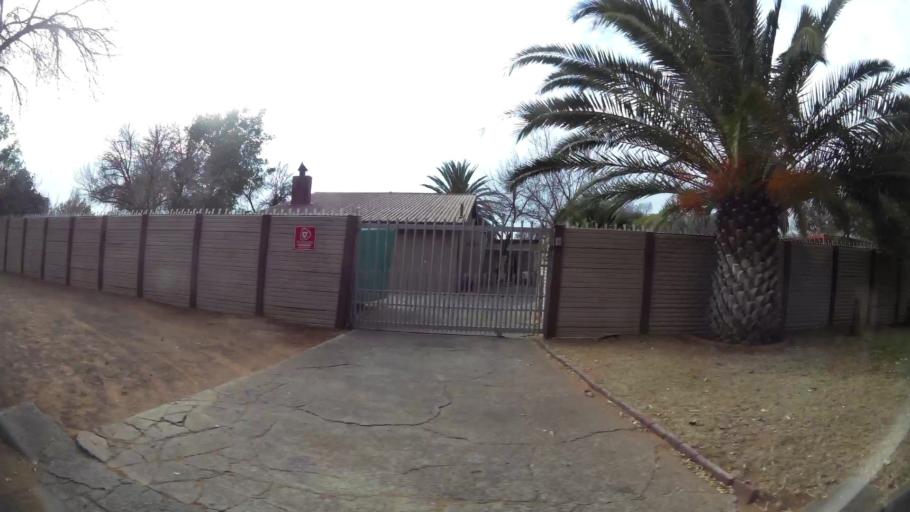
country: ZA
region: Orange Free State
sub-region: Mangaung Metropolitan Municipality
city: Bloemfontein
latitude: -29.1207
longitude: 26.1820
